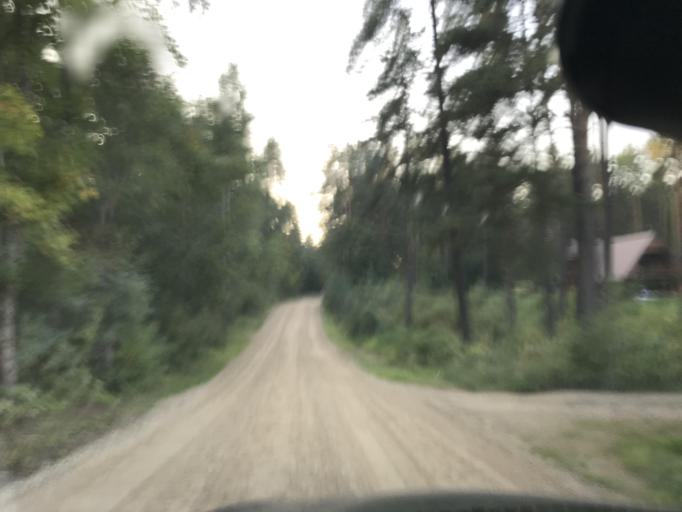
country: LV
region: Ikskile
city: Ikskile
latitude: 56.8294
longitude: 24.5117
